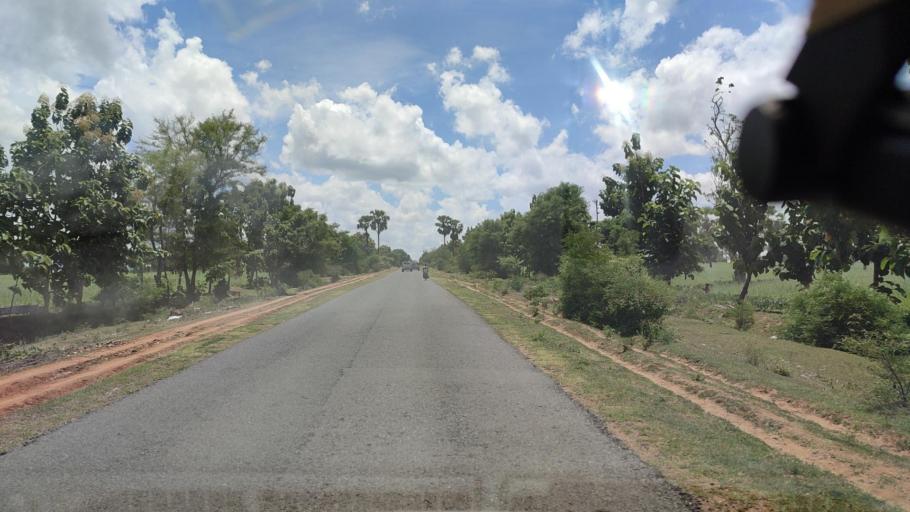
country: MM
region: Magway
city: Magway
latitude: 20.1905
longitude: 95.1794
